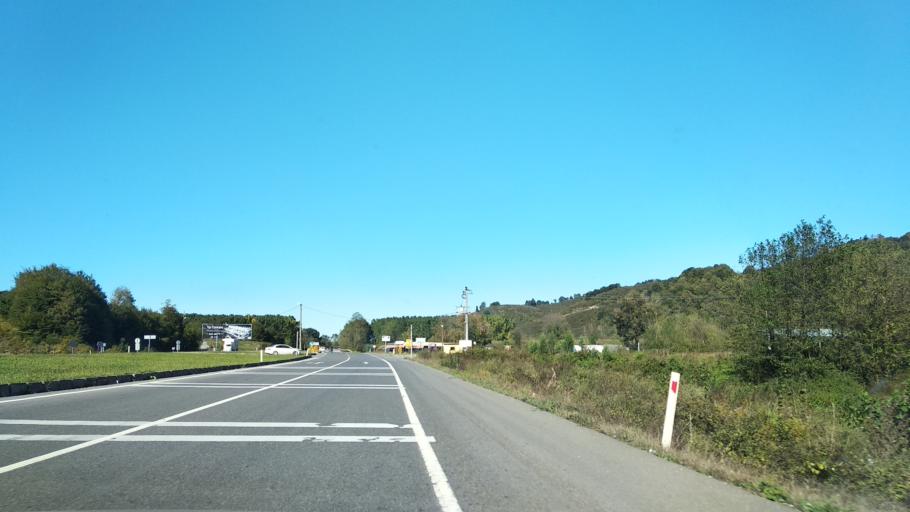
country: TR
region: Sakarya
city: Karasu
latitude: 41.0533
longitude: 30.6353
